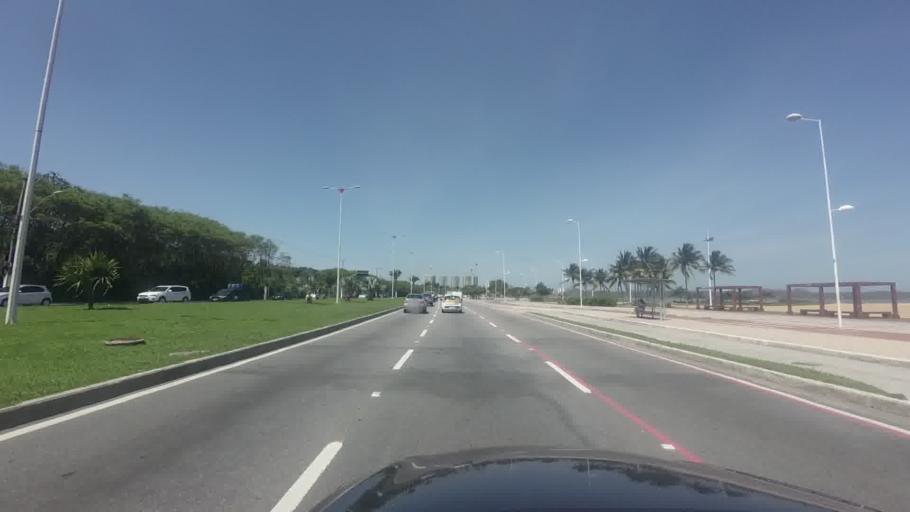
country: BR
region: Espirito Santo
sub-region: Vila Velha
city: Vila Velha
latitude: -20.2734
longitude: -40.2805
